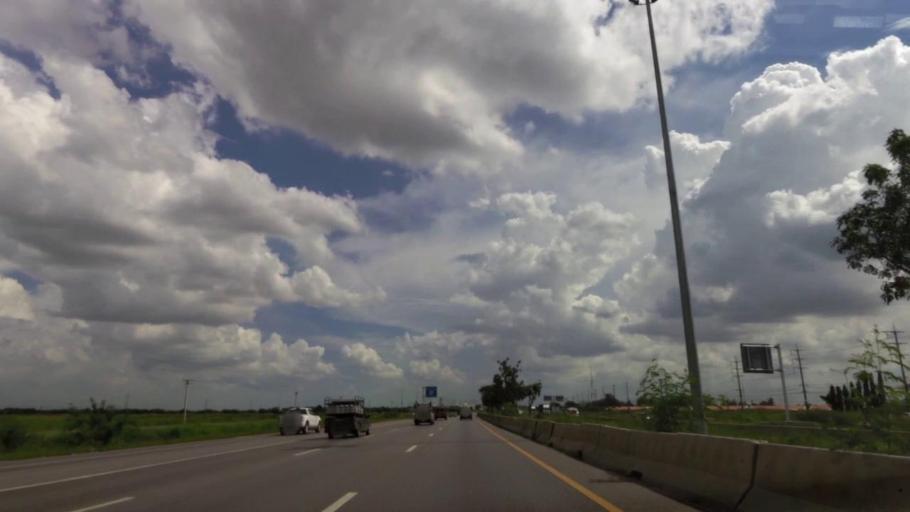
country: TH
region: Phra Nakhon Si Ayutthaya
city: Phra Nakhon Si Ayutthaya
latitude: 14.3910
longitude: 100.5992
